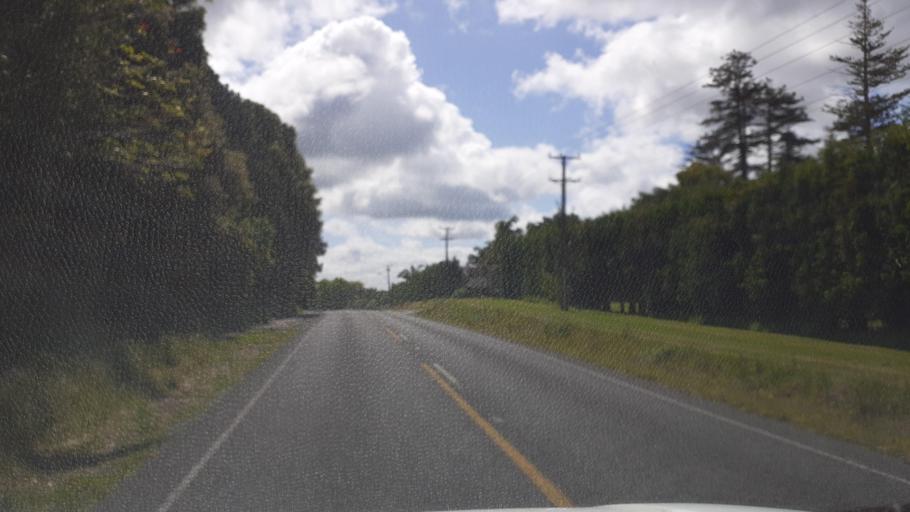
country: NZ
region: Northland
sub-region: Far North District
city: Kerikeri
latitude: -35.2232
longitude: 173.9745
